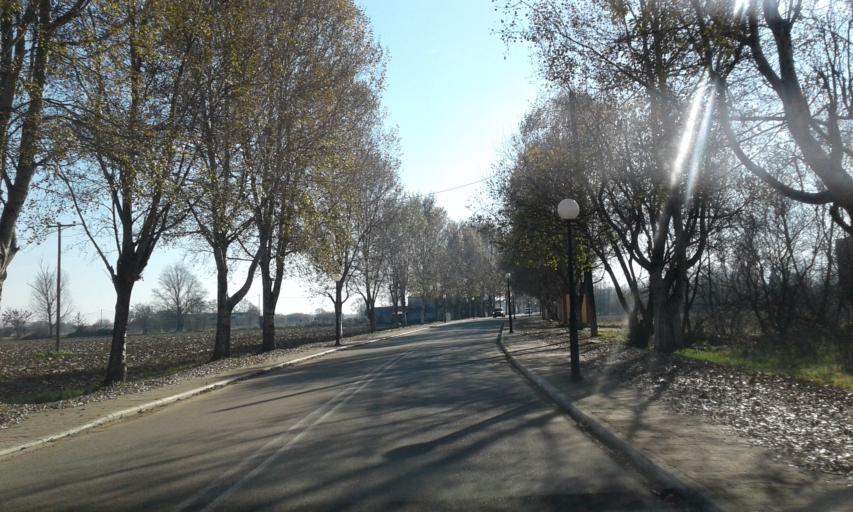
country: GR
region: Central Macedonia
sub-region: Nomos Thessalonikis
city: Lagkadas
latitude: 40.7397
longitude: 23.0802
